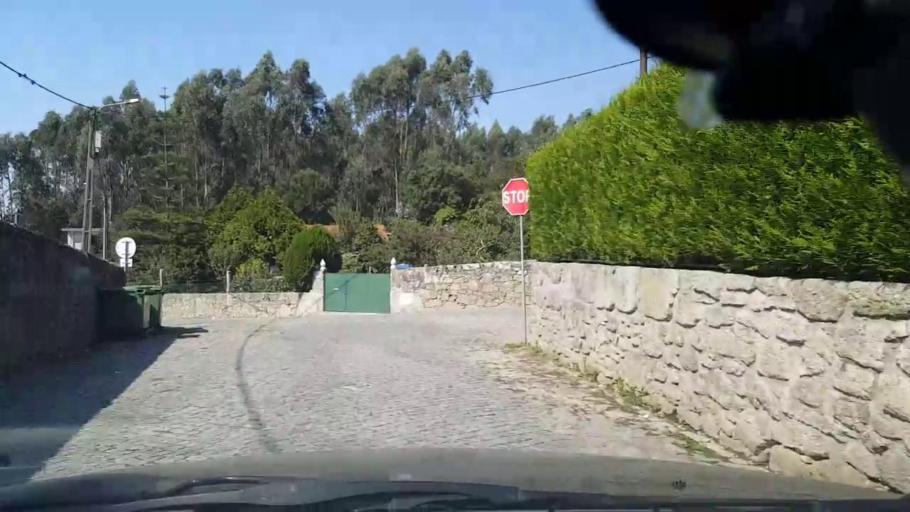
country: PT
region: Porto
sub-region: Vila do Conde
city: Arvore
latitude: 41.3810
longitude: -8.7062
